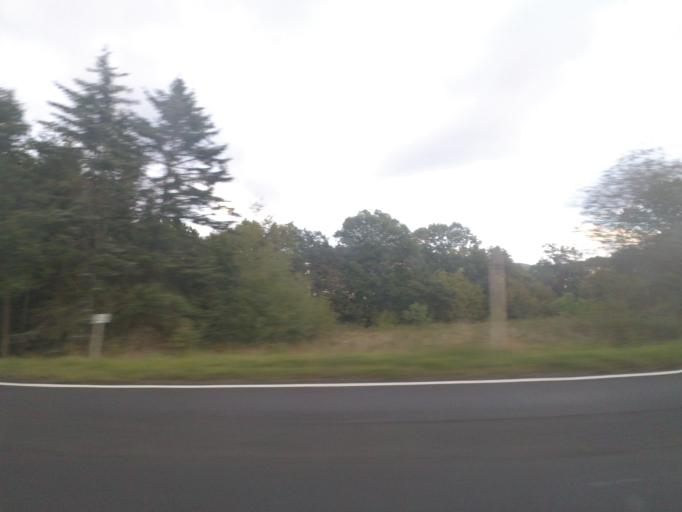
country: DE
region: Bavaria
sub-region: Regierungsbezirk Unterfranken
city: Bad Bruckenau
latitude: 50.3030
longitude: 9.7820
